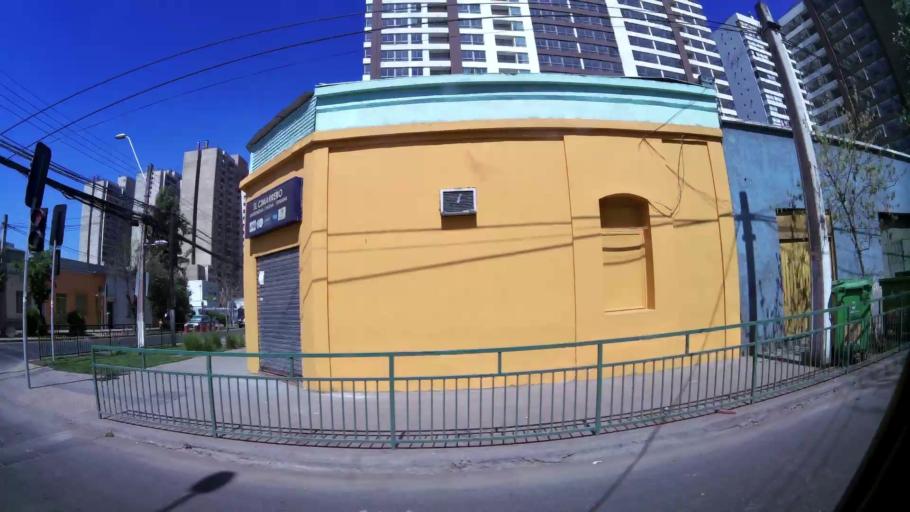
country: CL
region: Santiago Metropolitan
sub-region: Provincia de Santiago
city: Santiago
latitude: -33.4652
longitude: -70.6286
